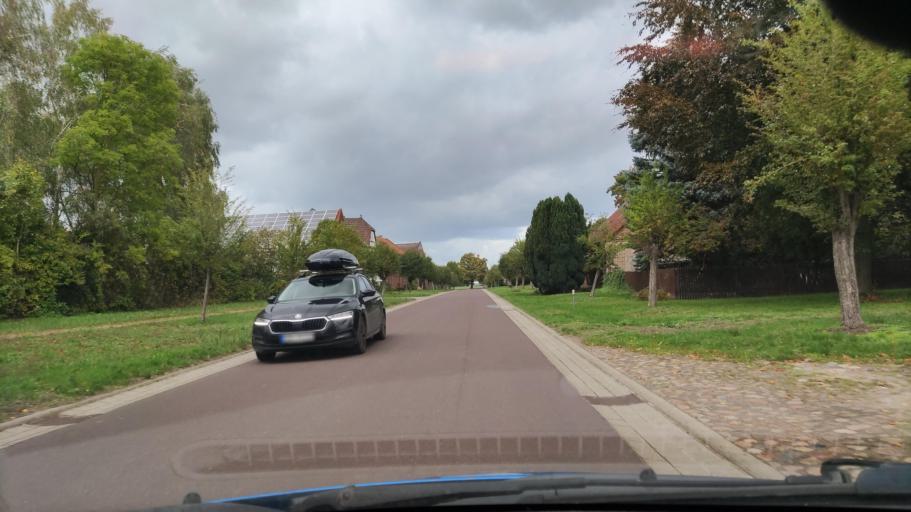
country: DE
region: Saxony-Anhalt
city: Luftkurort Arendsee
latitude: 52.8296
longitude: 11.3936
